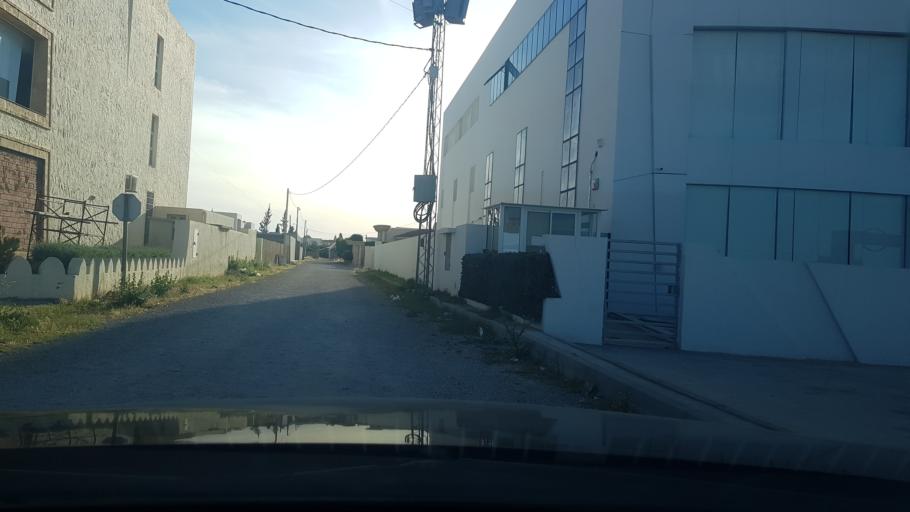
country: TN
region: Safaqis
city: Al Qarmadah
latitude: 34.8295
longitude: 10.7641
